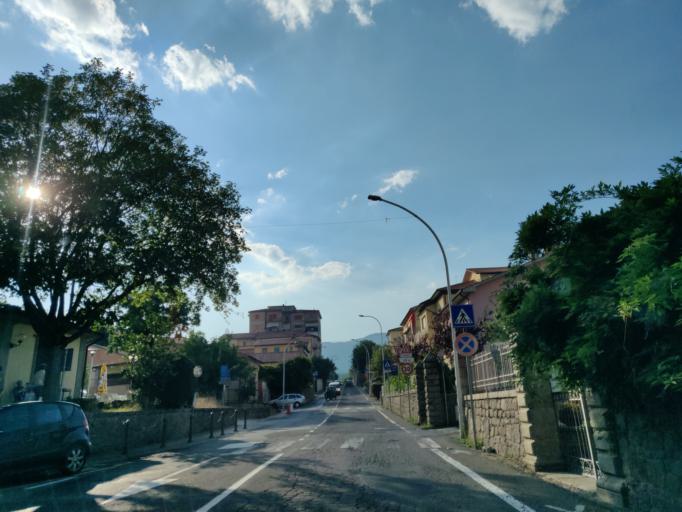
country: IT
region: Tuscany
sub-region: Provincia di Siena
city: Piancastagnaio
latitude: 42.8499
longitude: 11.6923
